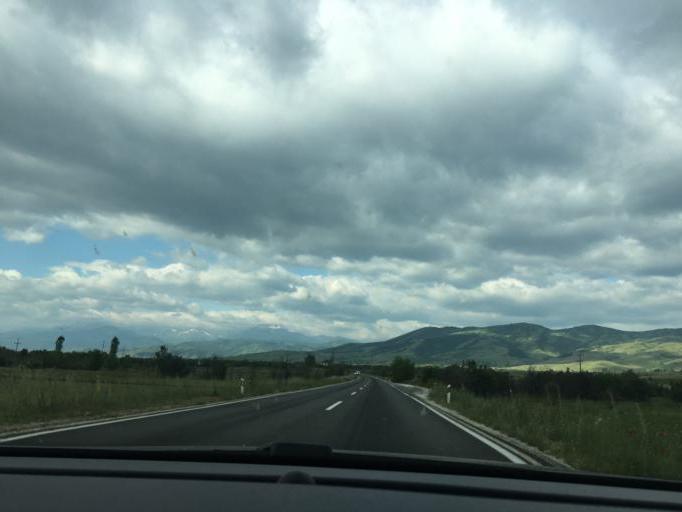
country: MK
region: Mogila
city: Dolno Srpci
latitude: 41.1782
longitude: 21.3961
